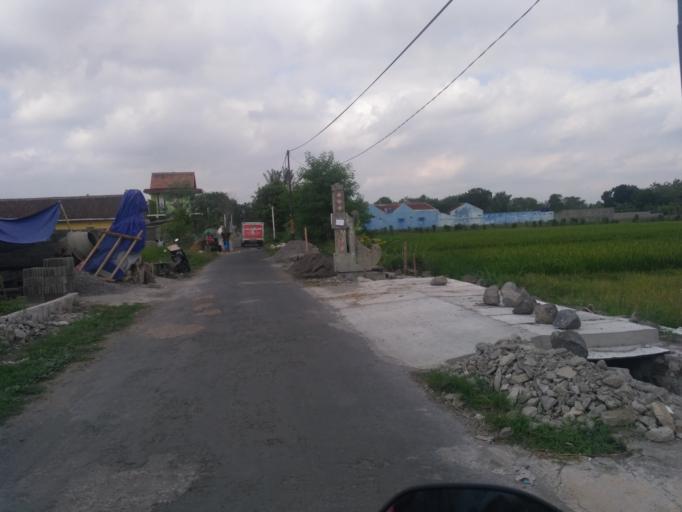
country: ID
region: Daerah Istimewa Yogyakarta
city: Melati
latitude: -7.7497
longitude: 110.3558
